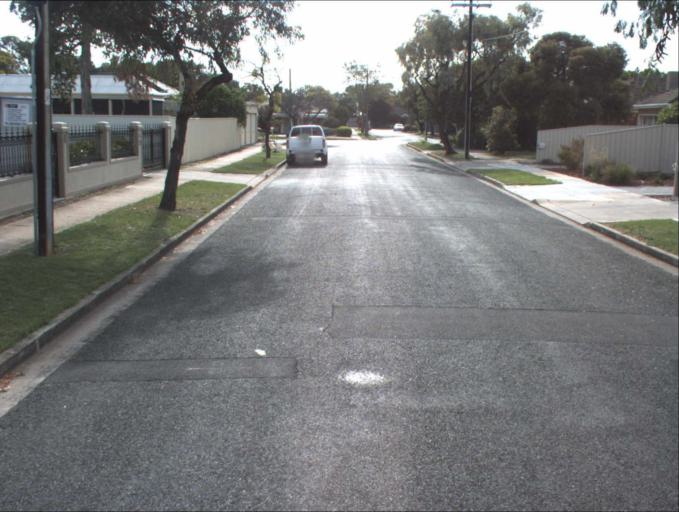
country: AU
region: South Australia
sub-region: Port Adelaide Enfield
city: Klemzig
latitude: -34.8746
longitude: 138.6224
